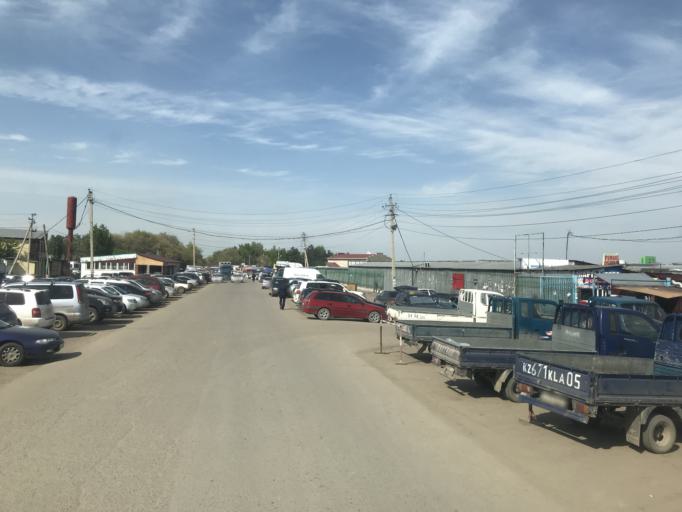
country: KZ
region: Almaty Oblysy
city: Burunday
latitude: 43.2313
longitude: 76.7698
